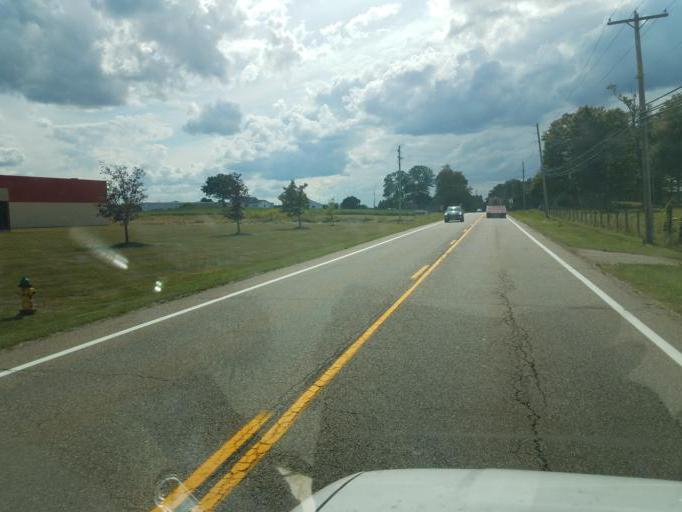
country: US
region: Ohio
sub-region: Portage County
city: Ravenna
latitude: 41.1848
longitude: -81.2192
